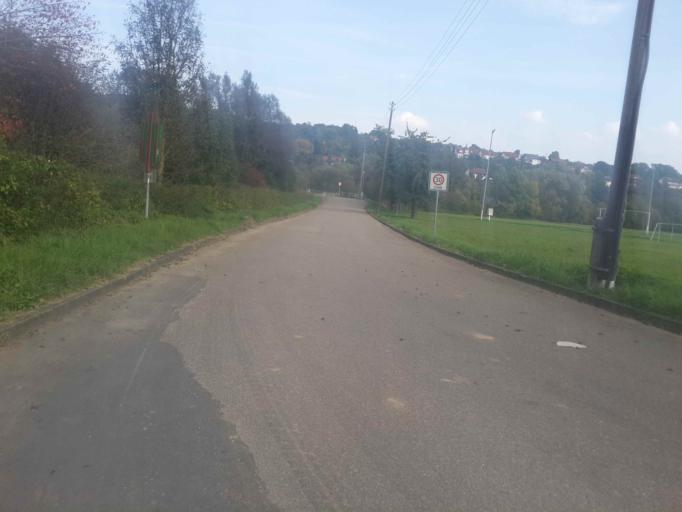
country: DE
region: Baden-Wuerttemberg
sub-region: Regierungsbezirk Stuttgart
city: Widdern
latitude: 49.3104
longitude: 9.4419
